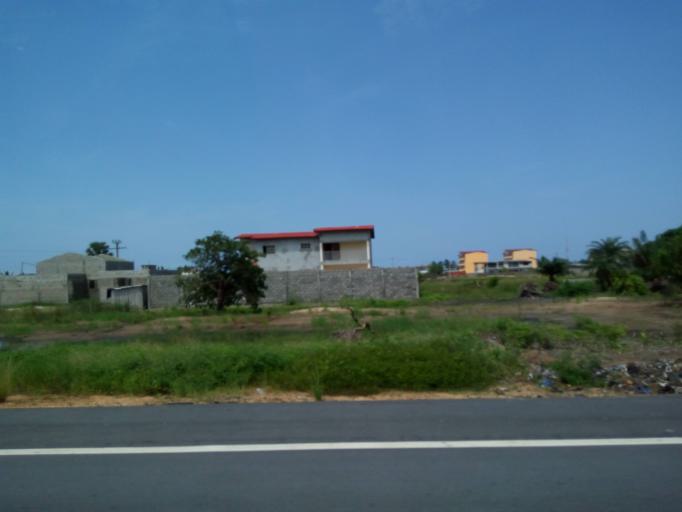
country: CI
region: Sud-Comoe
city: Grand-Bassam
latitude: 5.2251
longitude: -3.7337
